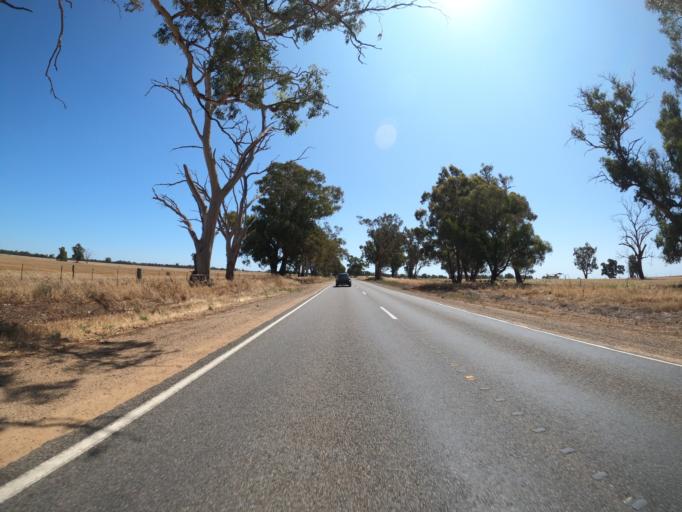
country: AU
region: Victoria
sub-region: Moira
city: Yarrawonga
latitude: -36.0247
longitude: 146.1055
